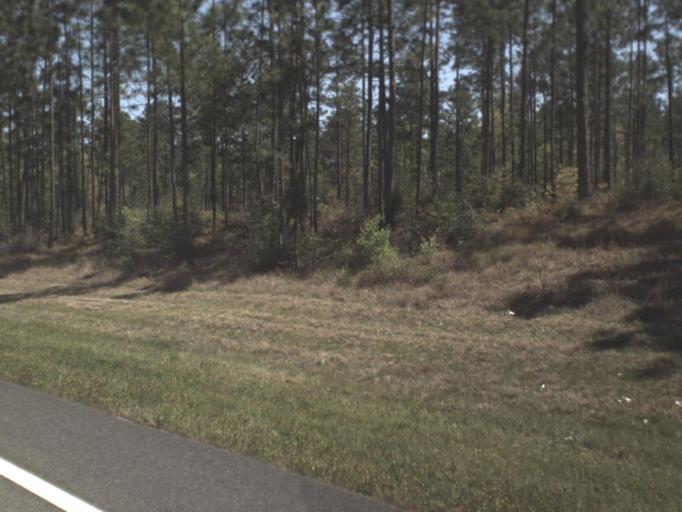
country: US
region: Florida
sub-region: Okaloosa County
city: Crestview
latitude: 30.8507
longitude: -86.7967
